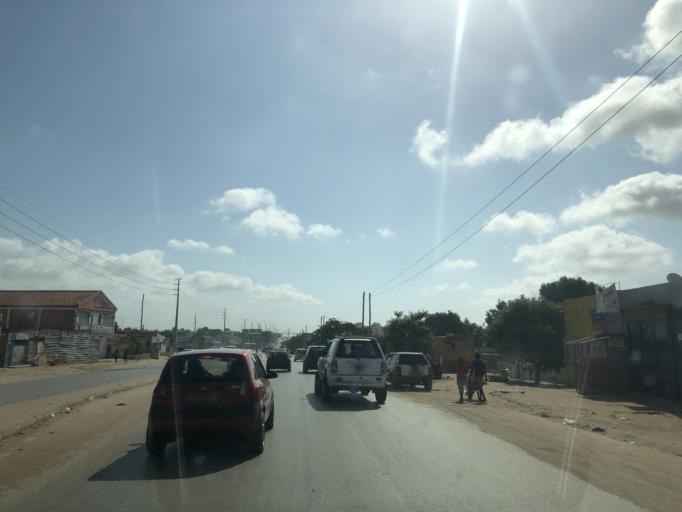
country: AO
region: Luanda
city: Luanda
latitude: -8.9046
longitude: 13.2462
